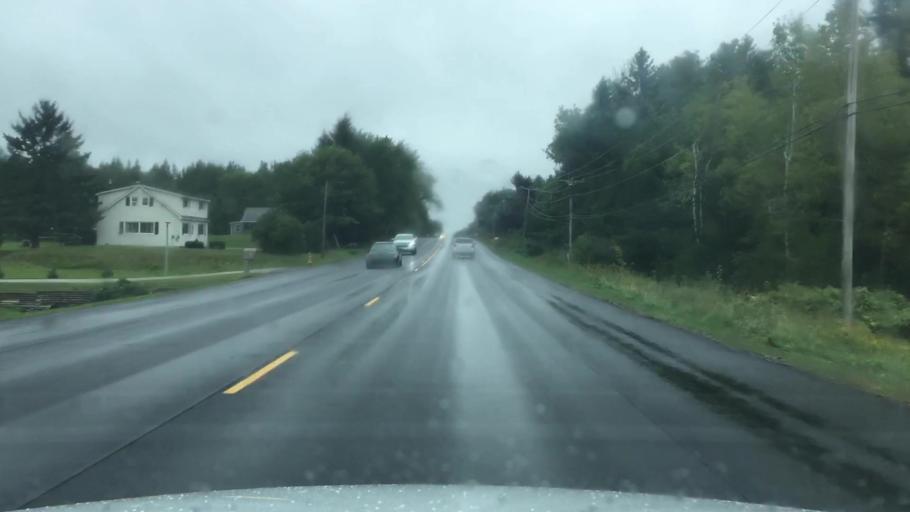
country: US
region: Maine
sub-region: Penobscot County
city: Hampden
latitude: 44.7643
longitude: -68.8517
